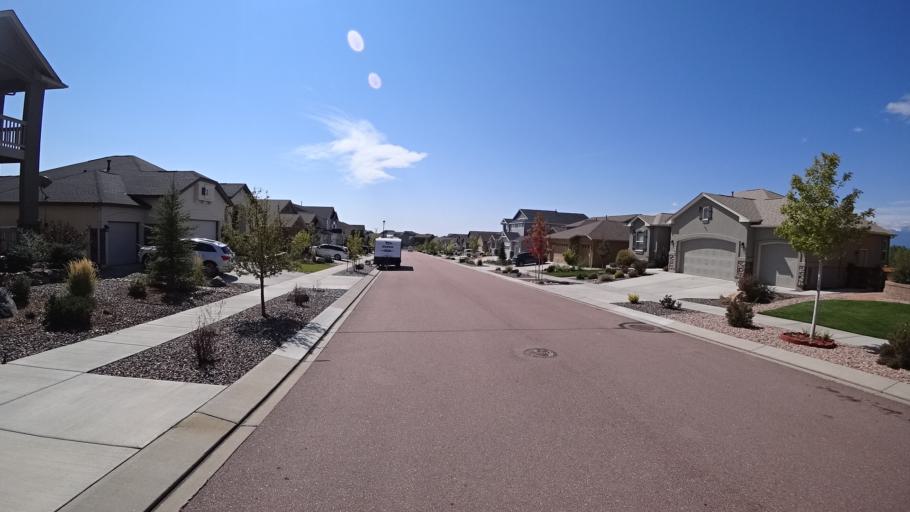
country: US
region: Colorado
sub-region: El Paso County
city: Cimarron Hills
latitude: 38.9340
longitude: -104.6857
